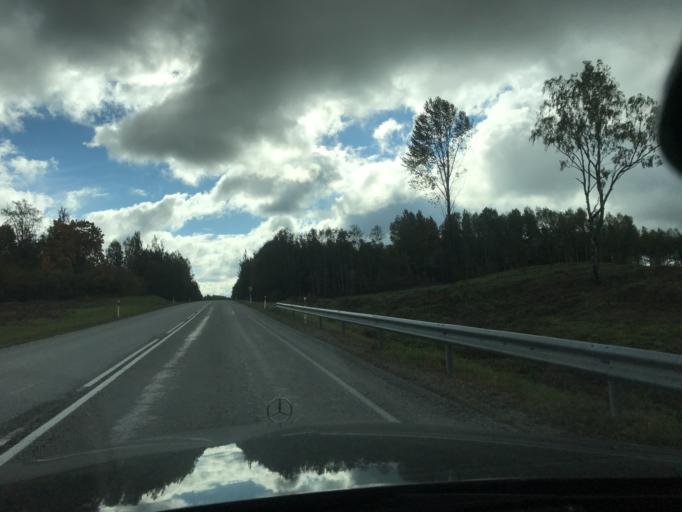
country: RU
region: Pskov
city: Pechory
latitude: 57.7012
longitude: 27.3250
